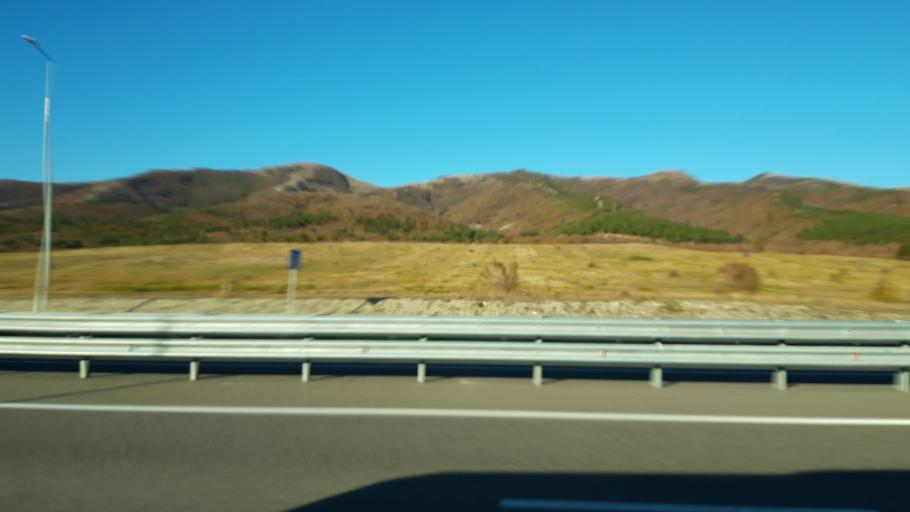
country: RU
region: Krasnodarskiy
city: Kabardinka
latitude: 44.6445
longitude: 37.9668
